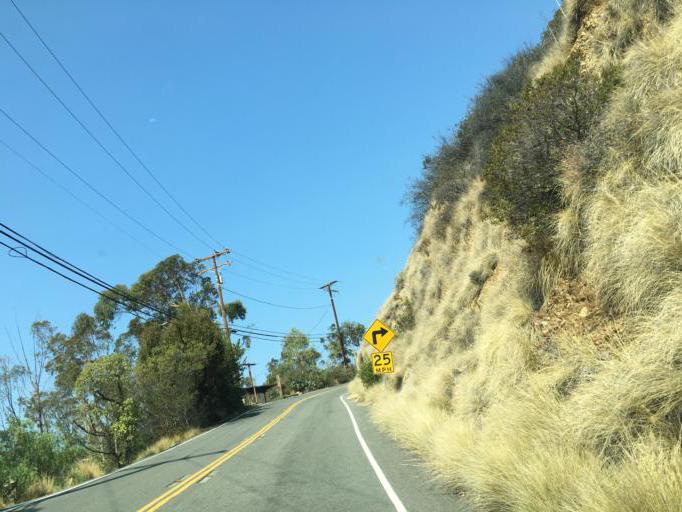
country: US
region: California
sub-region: Los Angeles County
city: Las Flores
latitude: 34.0541
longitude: -118.6515
